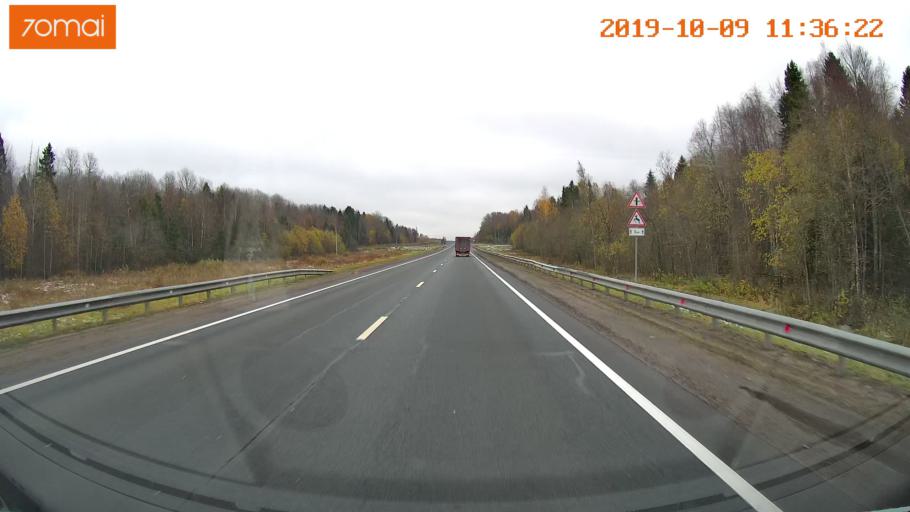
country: RU
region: Vologda
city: Gryazovets
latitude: 58.9916
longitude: 40.1359
